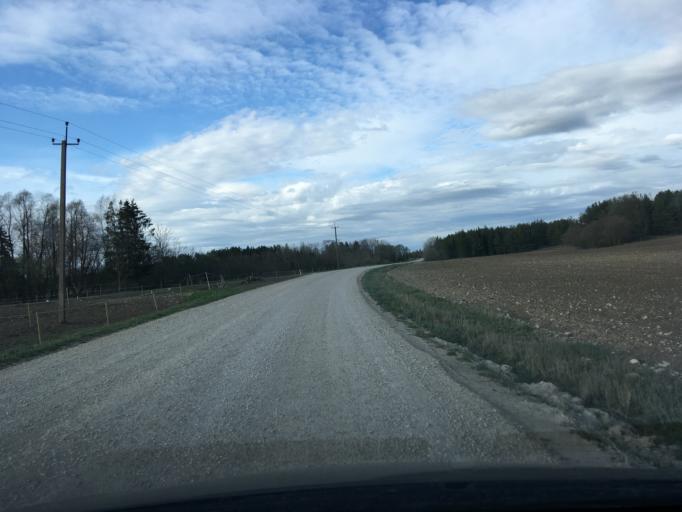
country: EE
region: Raplamaa
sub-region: Maerjamaa vald
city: Marjamaa
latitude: 58.9379
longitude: 24.3096
